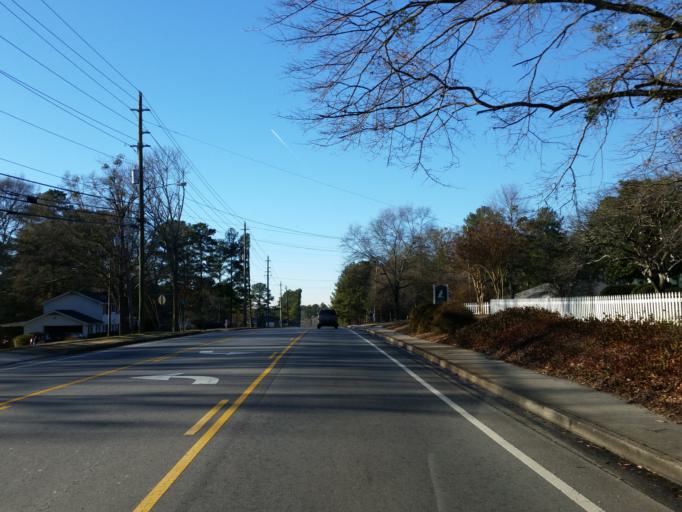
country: US
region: Georgia
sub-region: Cobb County
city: Kennesaw
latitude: 33.9643
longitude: -84.6614
